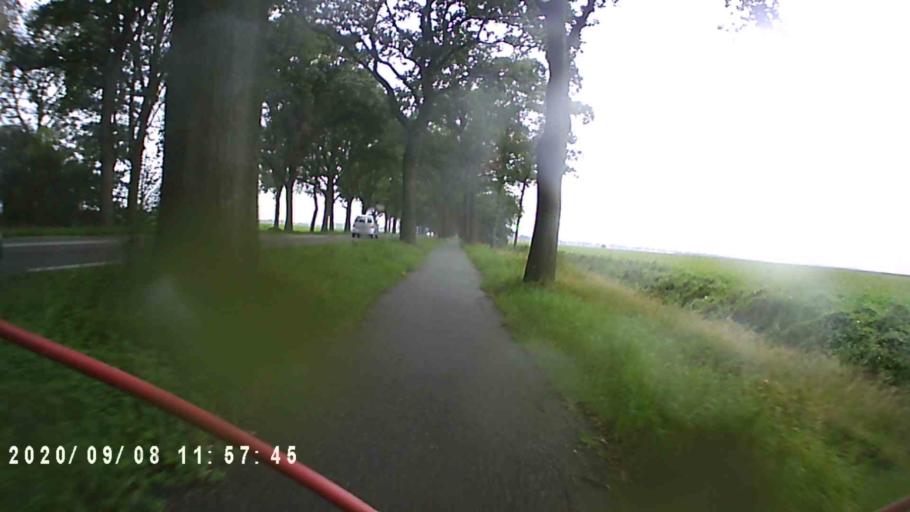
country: NL
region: Groningen
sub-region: Gemeente Veendam
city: Veendam
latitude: 53.1089
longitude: 6.8218
